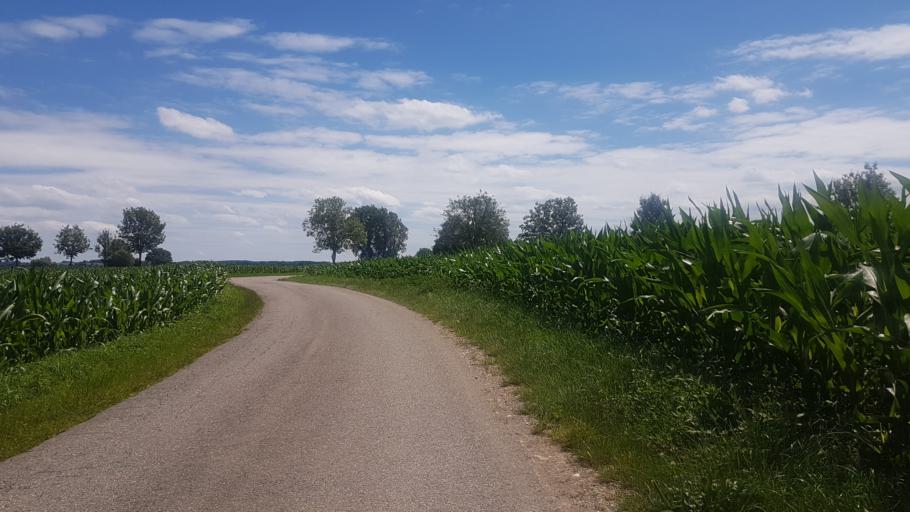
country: DE
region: Bavaria
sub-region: Swabia
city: Buttenwiesen
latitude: 48.6320
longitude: 10.6912
